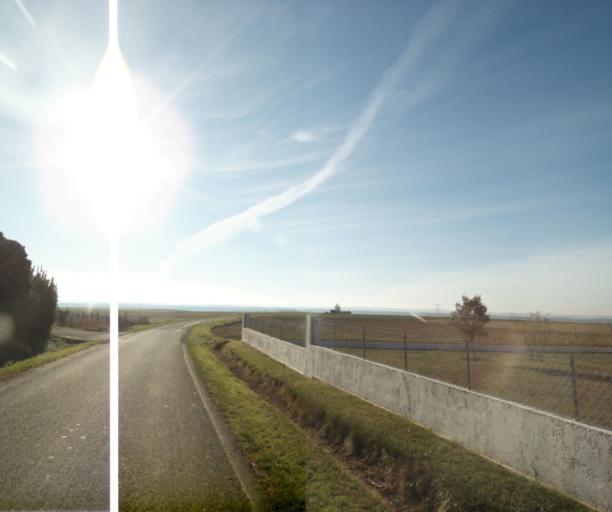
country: FR
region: Poitou-Charentes
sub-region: Departement de la Charente-Maritime
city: Chaniers
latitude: 45.7356
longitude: -0.5752
